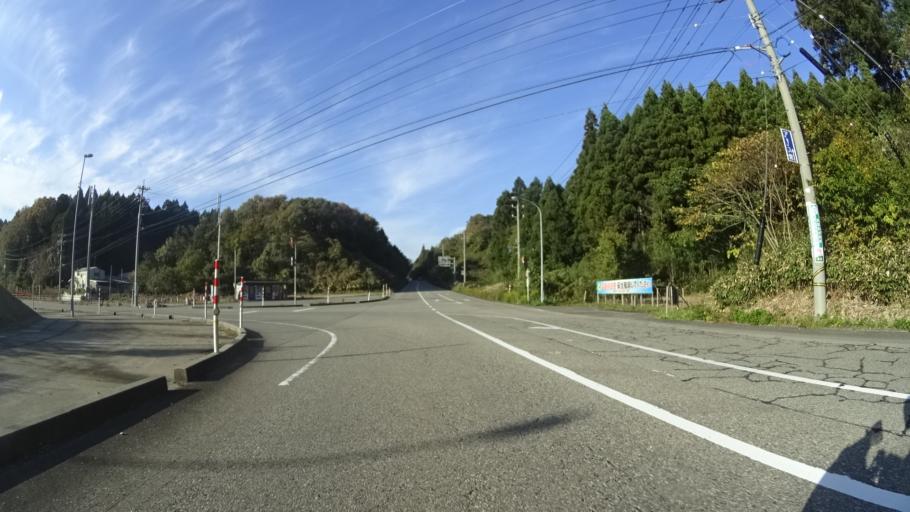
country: JP
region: Ishikawa
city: Hakui
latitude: 37.0082
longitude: 136.7998
